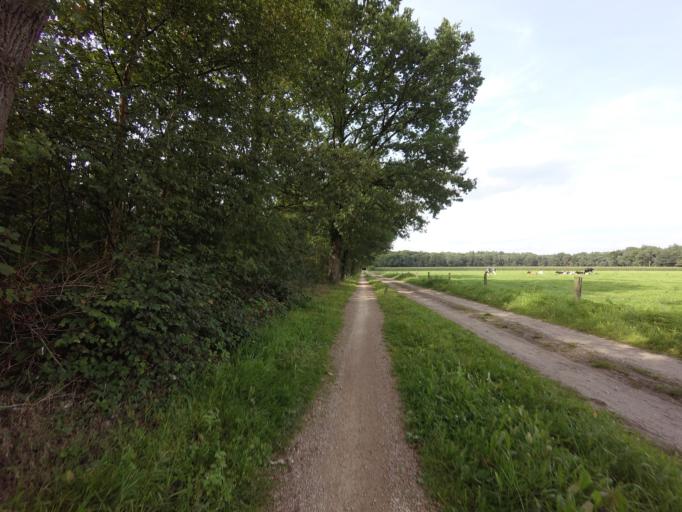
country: DE
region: Lower Saxony
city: Getelo
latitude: 52.4319
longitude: 6.8705
